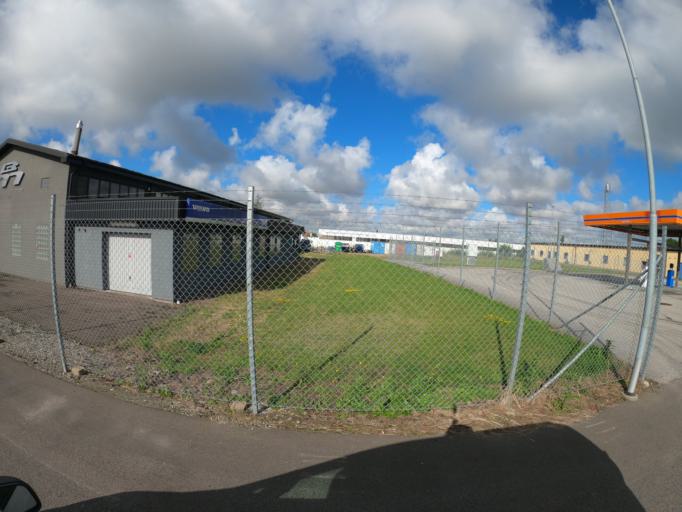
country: SE
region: Skane
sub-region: Lunds Kommun
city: Genarp
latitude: 55.6053
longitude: 13.4007
